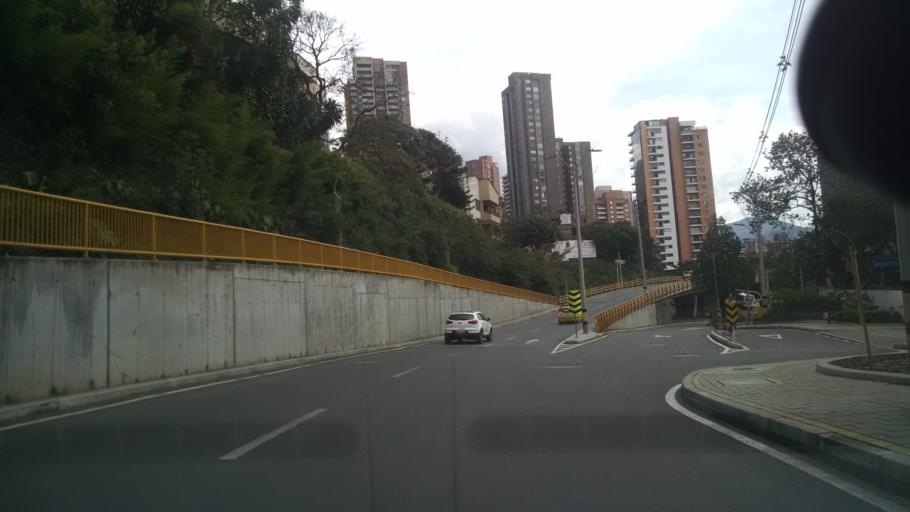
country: CO
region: Antioquia
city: Medellin
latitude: 6.2099
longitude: -75.5589
